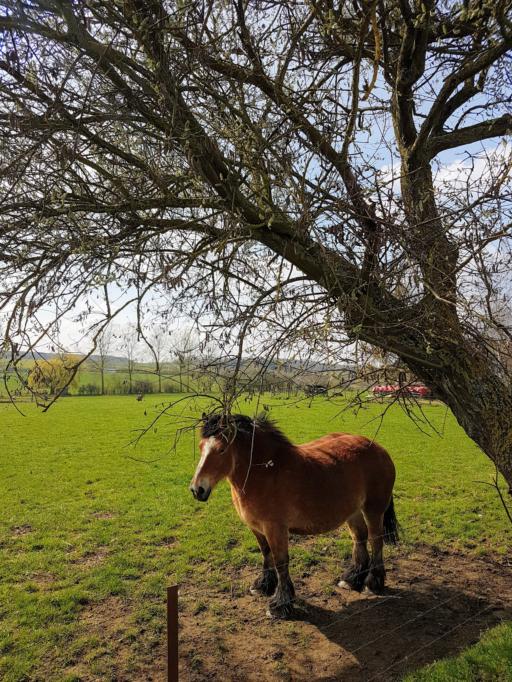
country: LU
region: Luxembourg
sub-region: Canton de Luxembourg
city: Luxembourg
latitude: 49.5825
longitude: 6.1081
